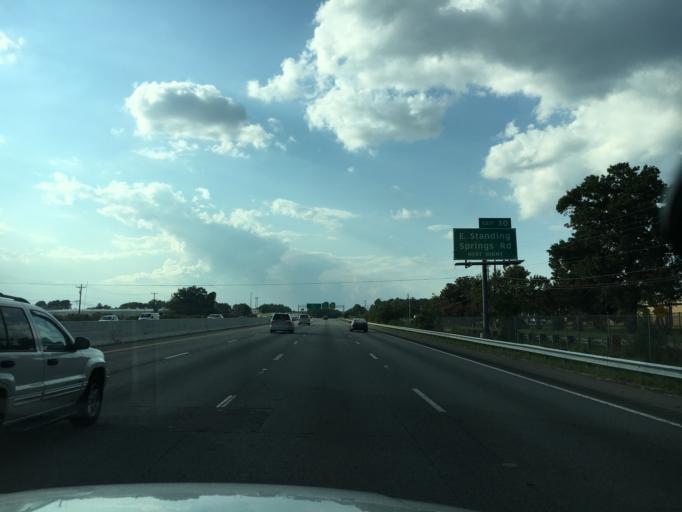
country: US
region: South Carolina
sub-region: Greenville County
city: Simpsonville
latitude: 34.7463
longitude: -82.2797
